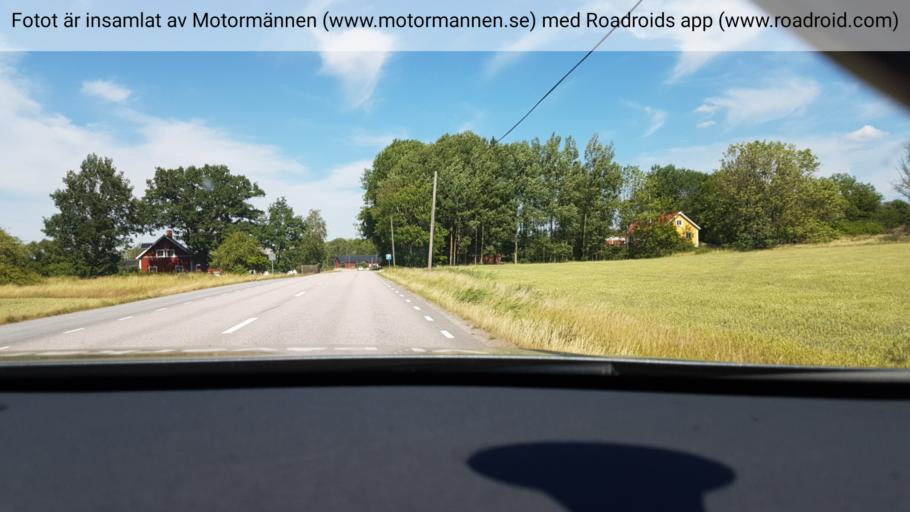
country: SE
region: Vaestra Goetaland
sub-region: Skovde Kommun
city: Stopen
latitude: 58.5096
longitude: 13.9731
